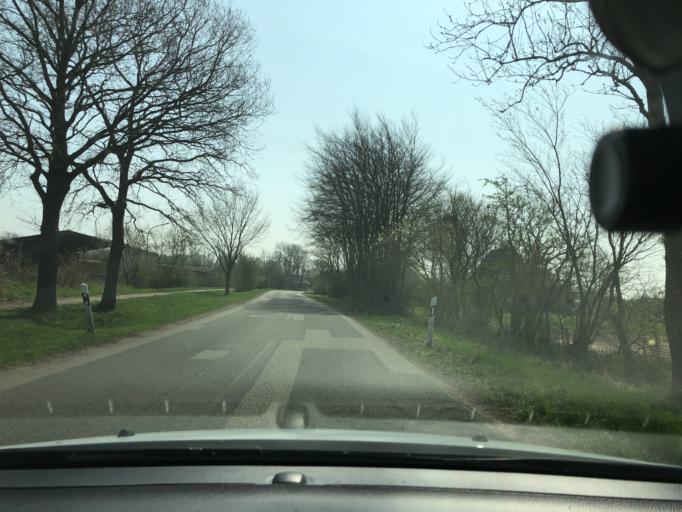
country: DE
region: Schleswig-Holstein
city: Grossenwiehe
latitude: 54.6914
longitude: 9.2397
